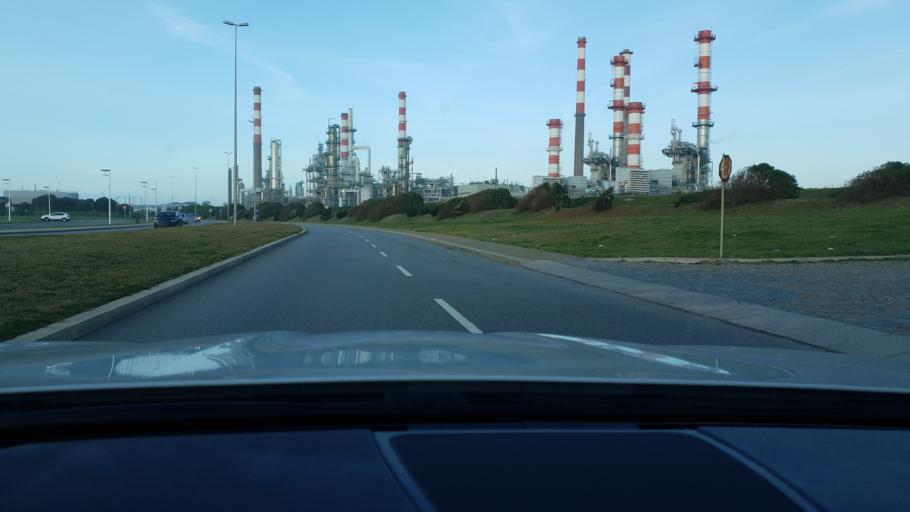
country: PT
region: Porto
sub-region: Matosinhos
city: Leca da Palmeira
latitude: 41.2085
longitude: -8.7141
